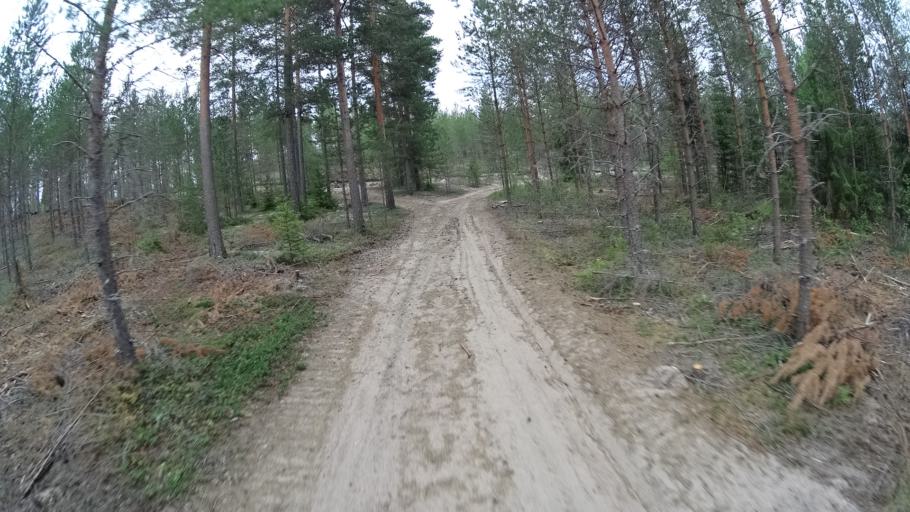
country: FI
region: Satakunta
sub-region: Pohjois-Satakunta
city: Jaemijaervi
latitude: 61.7693
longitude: 22.8215
